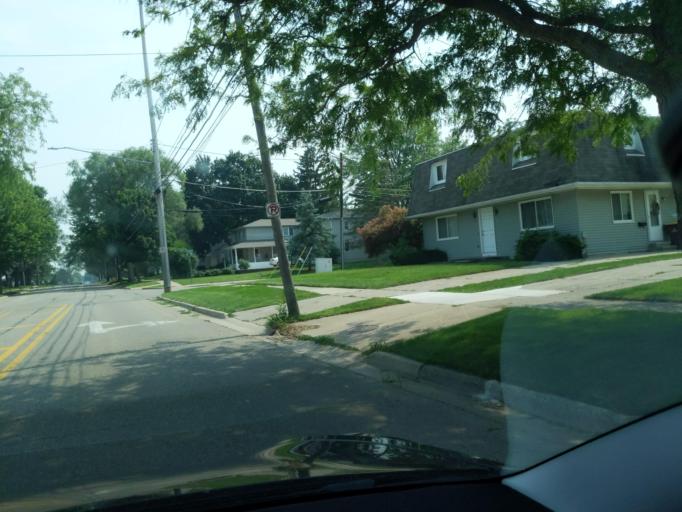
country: US
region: Michigan
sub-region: Clinton County
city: Saint Johns
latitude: 42.9934
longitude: -84.5625
